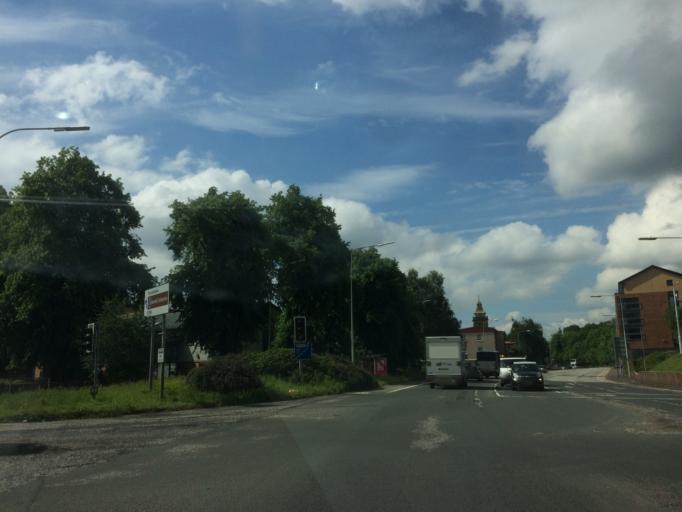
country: GB
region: Scotland
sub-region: East Renfrewshire
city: Giffnock
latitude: 55.8276
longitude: -4.2960
